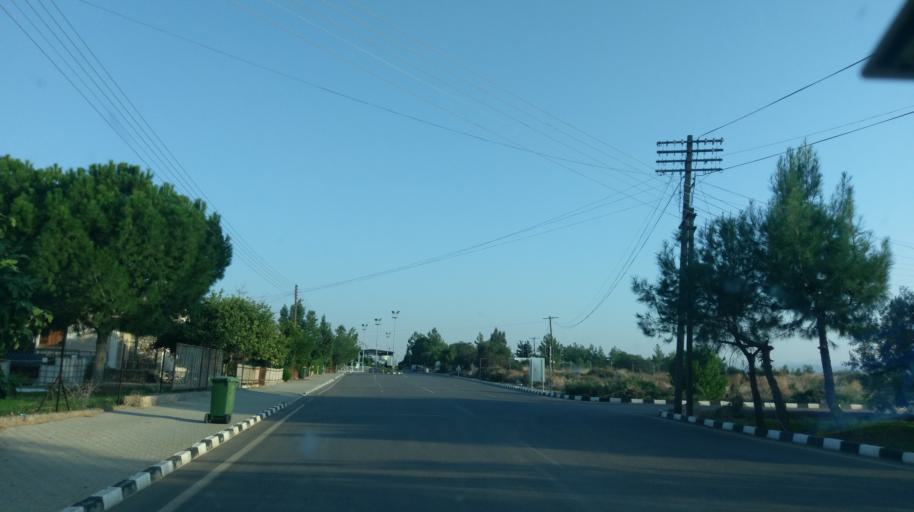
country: CY
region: Lefkosia
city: Astromeritis
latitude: 35.1593
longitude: 33.0181
